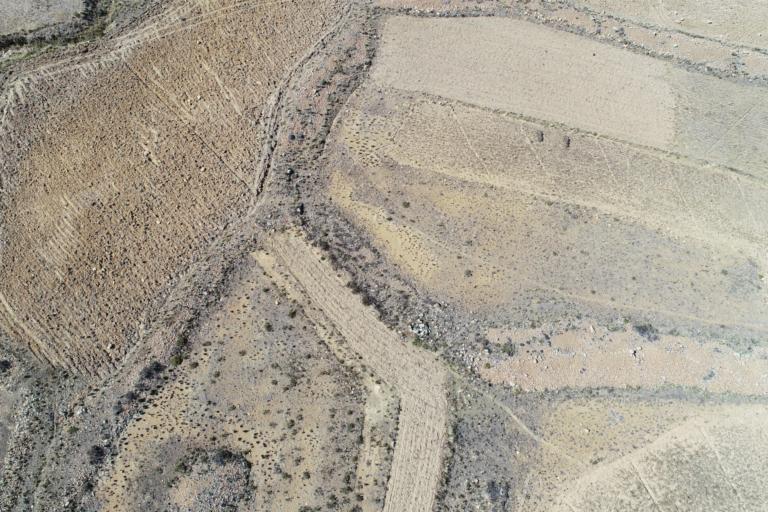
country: BO
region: La Paz
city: Achacachi
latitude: -15.8840
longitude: -68.8106
